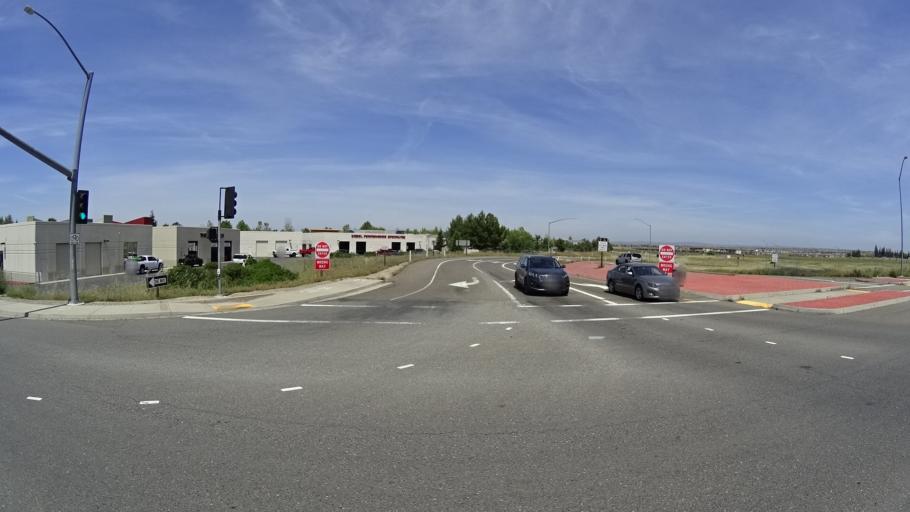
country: US
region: California
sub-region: Placer County
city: Roseville
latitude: 38.8174
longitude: -121.3020
